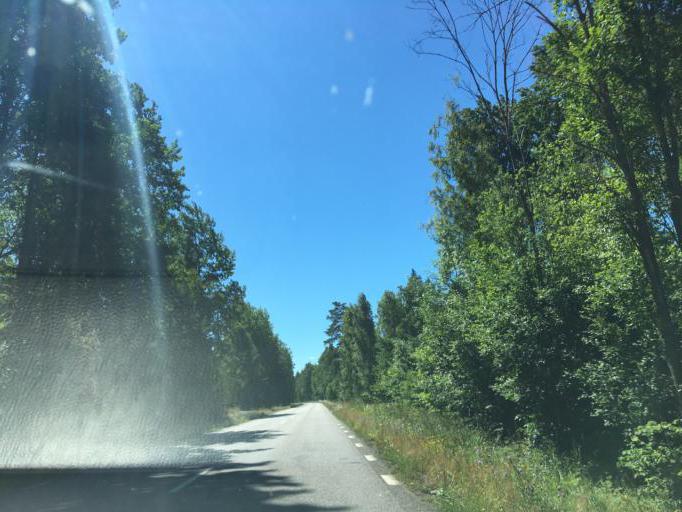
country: SE
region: OErebro
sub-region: Laxa Kommun
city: Laxa
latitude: 58.8281
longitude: 14.5462
